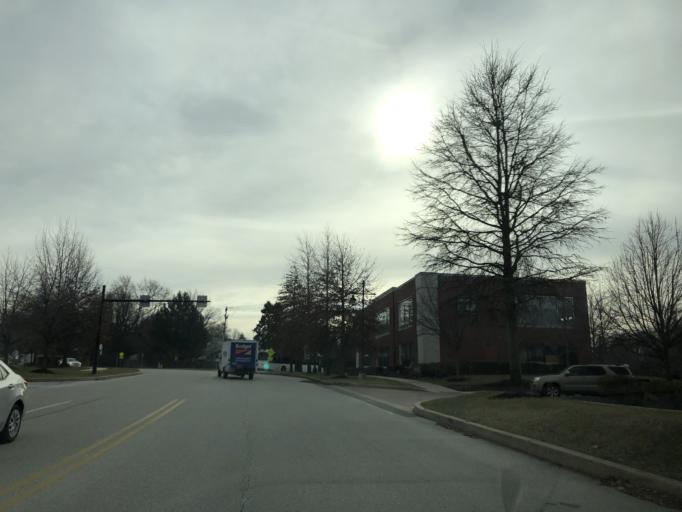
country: US
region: Pennsylvania
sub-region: Chester County
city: Exton
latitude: 40.0282
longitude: -75.6243
